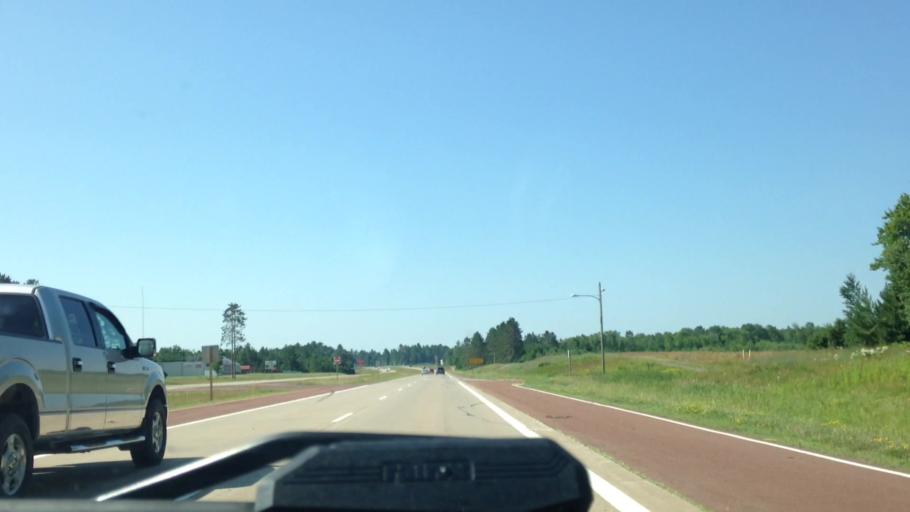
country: US
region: Wisconsin
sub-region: Douglas County
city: Lake Nebagamon
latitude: 46.3607
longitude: -91.8322
